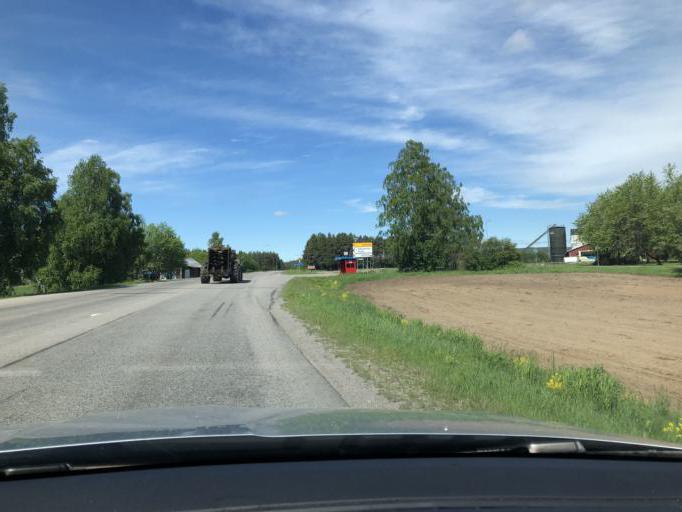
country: SE
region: Norrbotten
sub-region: Pitea Kommun
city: Bergsviken
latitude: 65.3539
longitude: 21.3851
